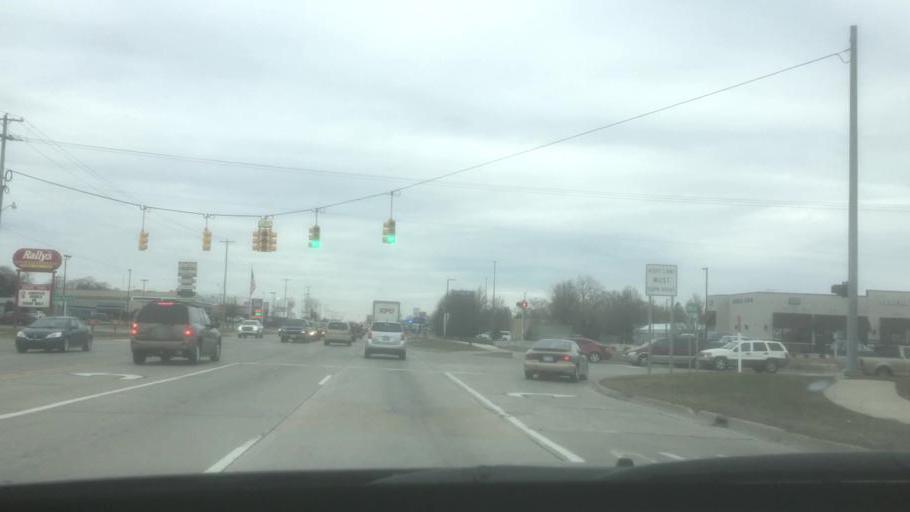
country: US
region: Michigan
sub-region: Bay County
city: Bay City
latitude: 43.6239
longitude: -83.8938
